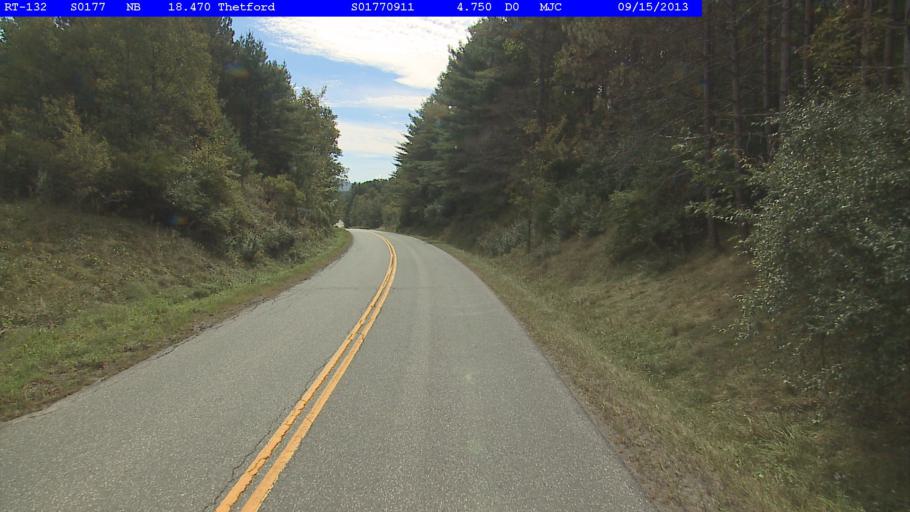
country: US
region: New Hampshire
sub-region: Grafton County
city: Hanover
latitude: 43.7920
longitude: -72.2628
